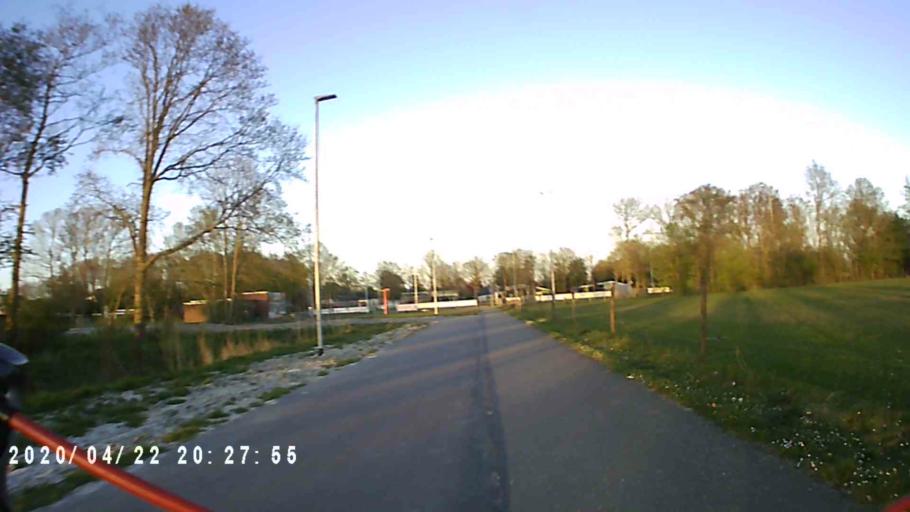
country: NL
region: Groningen
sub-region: Gemeente Winsum
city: Winsum
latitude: 53.3257
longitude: 6.5122
